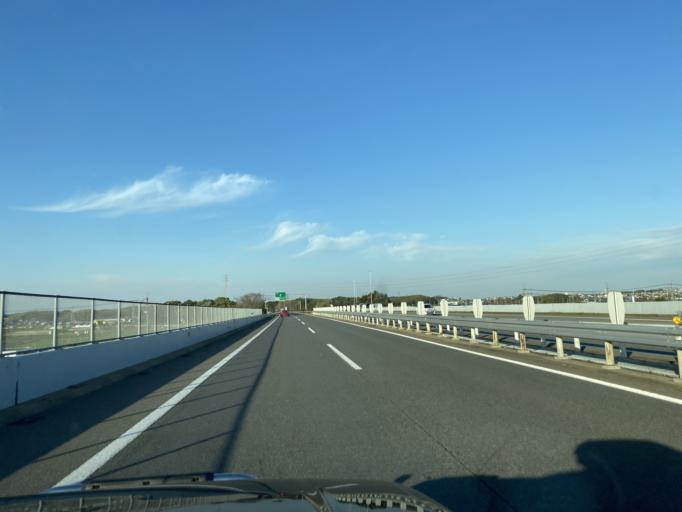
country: JP
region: Mie
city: Tsu-shi
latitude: 34.7337
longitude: 136.4705
